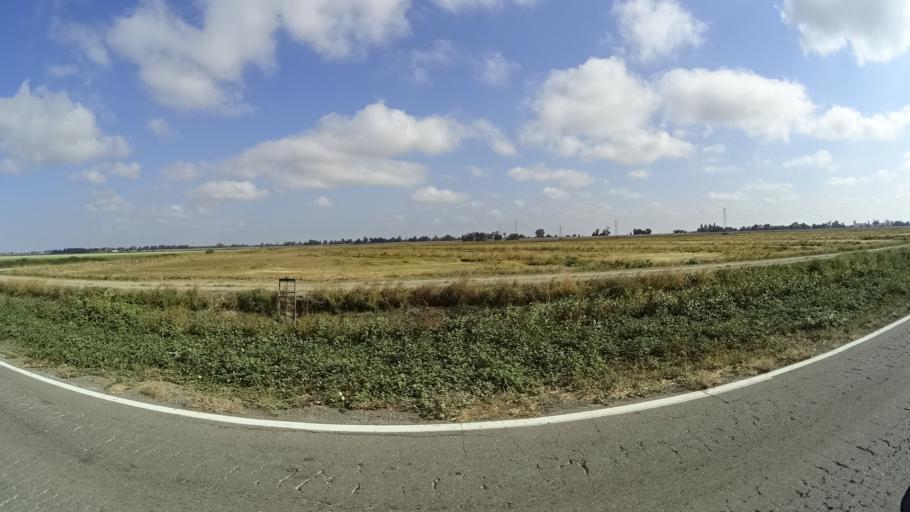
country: US
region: California
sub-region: Yolo County
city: Woodland
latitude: 38.8154
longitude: -121.7389
